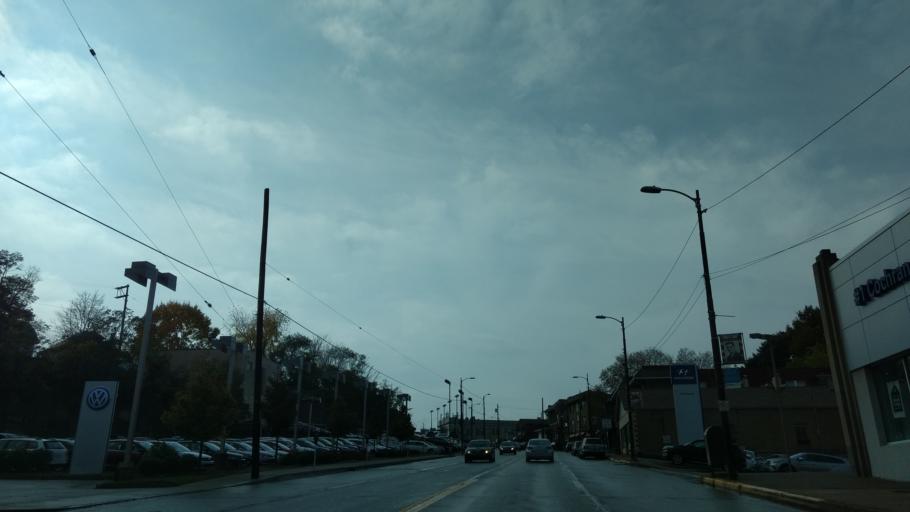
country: US
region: Pennsylvania
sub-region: Allegheny County
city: Dormont
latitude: 40.3968
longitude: -80.0308
